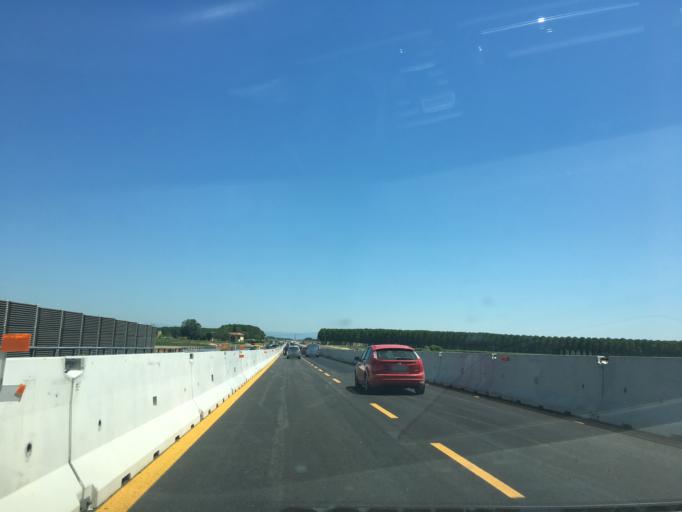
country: IT
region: Friuli Venezia Giulia
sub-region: Provincia di Udine
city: Muzzana del Turgnano
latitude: 45.8477
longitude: 13.1560
